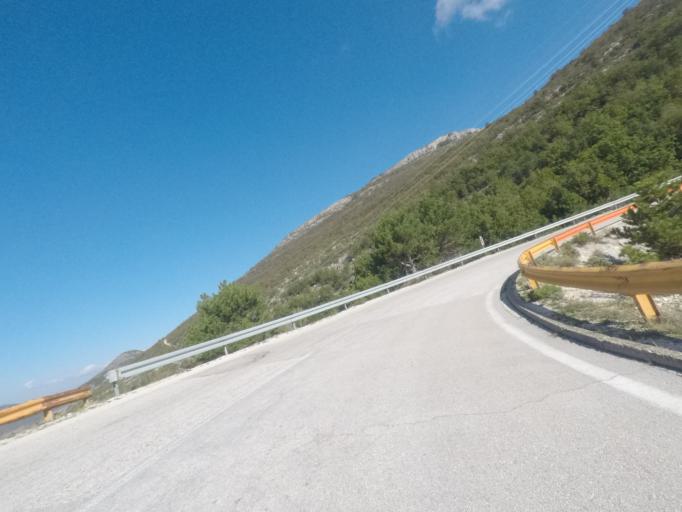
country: BA
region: Republika Srpska
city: Trebinje
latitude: 42.7161
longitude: 18.5263
